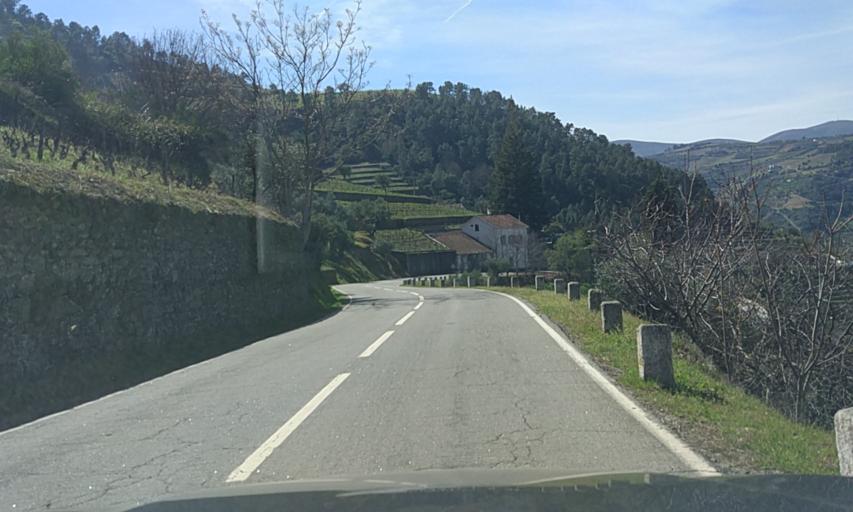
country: PT
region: Vila Real
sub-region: Sabrosa
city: Sabrosa
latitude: 41.2200
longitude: -7.5300
